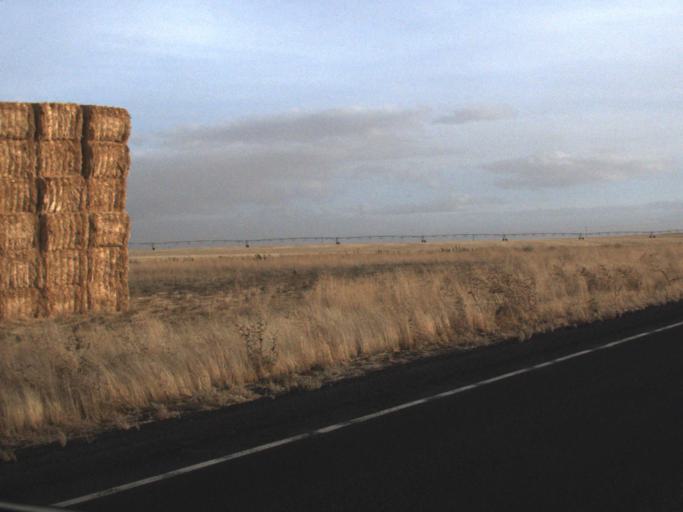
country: US
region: Washington
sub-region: Adams County
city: Ritzville
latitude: 47.1370
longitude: -118.6868
